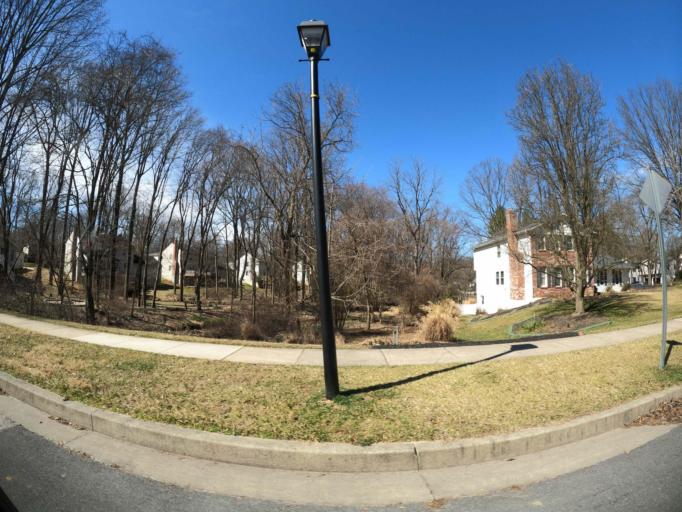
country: US
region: Maryland
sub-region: Howard County
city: Columbia
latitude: 39.2228
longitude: -76.8282
